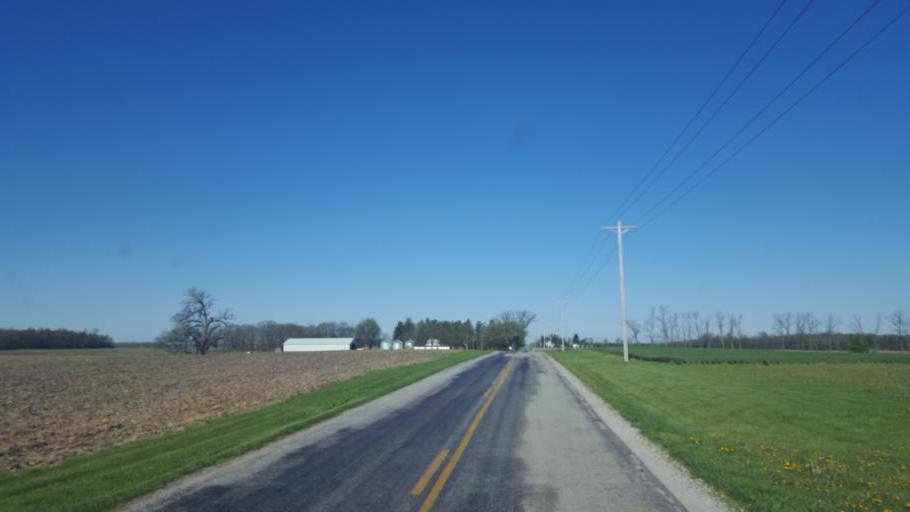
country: US
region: Ohio
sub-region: Marion County
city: Marion
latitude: 40.6740
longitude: -83.0257
